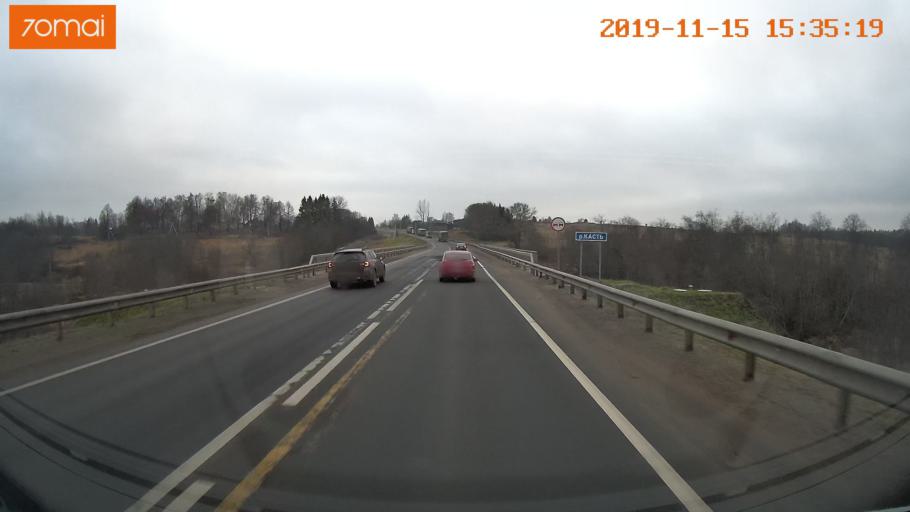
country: RU
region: Jaroslavl
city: Danilov
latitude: 58.0603
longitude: 40.0878
